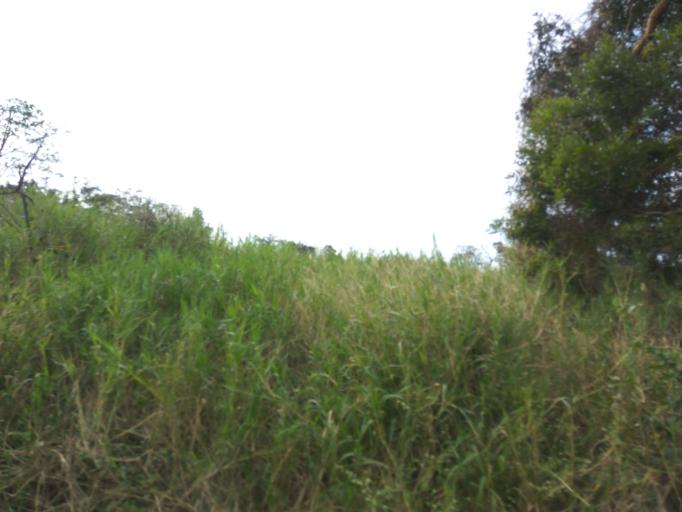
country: TW
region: Taiwan
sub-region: Hsinchu
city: Zhubei
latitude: 24.9694
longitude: 121.0148
